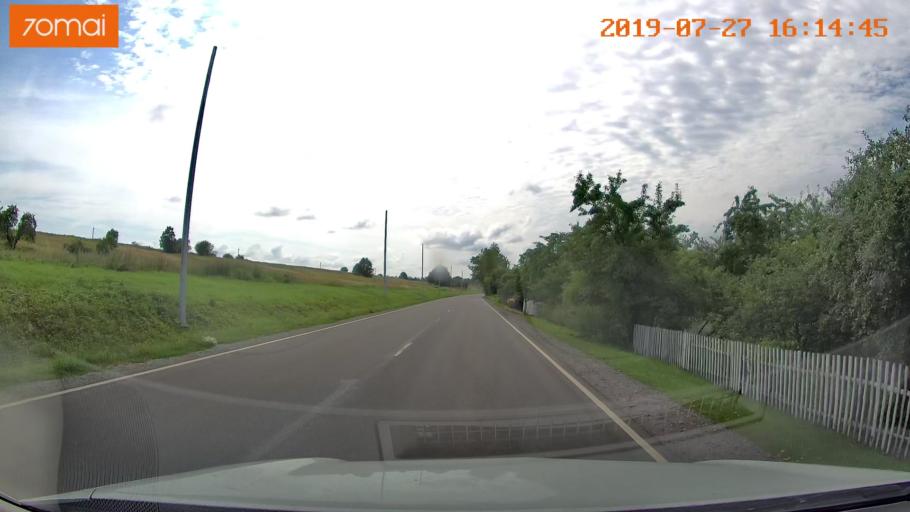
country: RU
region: Kaliningrad
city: Chernyakhovsk
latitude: 54.6261
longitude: 21.6127
